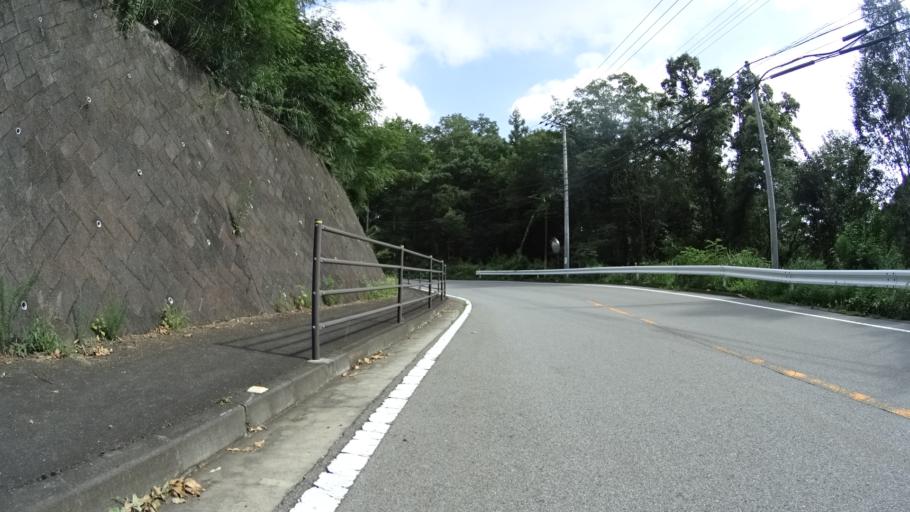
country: JP
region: Yamanashi
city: Kofu-shi
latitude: 35.7071
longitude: 138.5545
